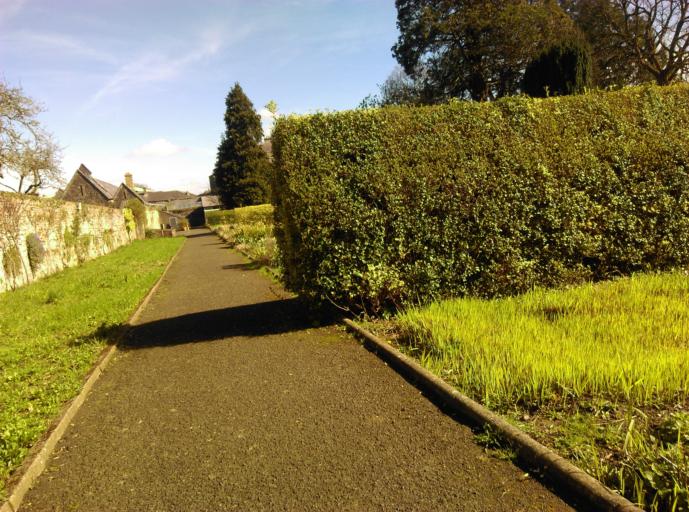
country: IE
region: Leinster
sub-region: Kildare
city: Maynooth
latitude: 53.3779
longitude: -6.5980
